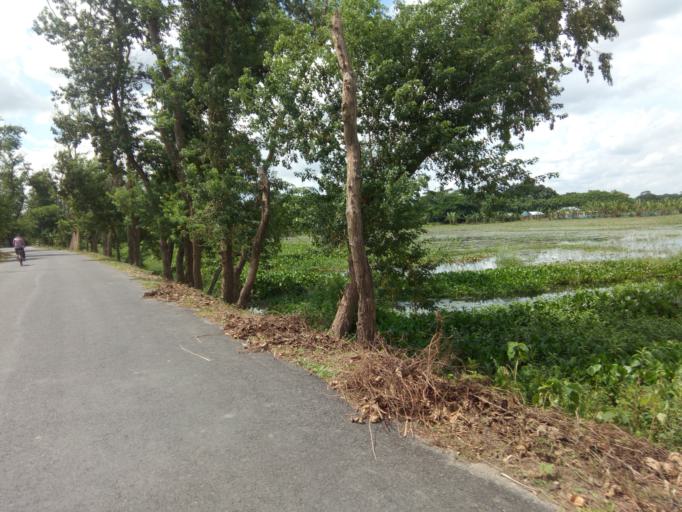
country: BD
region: Khulna
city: Kalia
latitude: 23.0143
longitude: 89.7231
